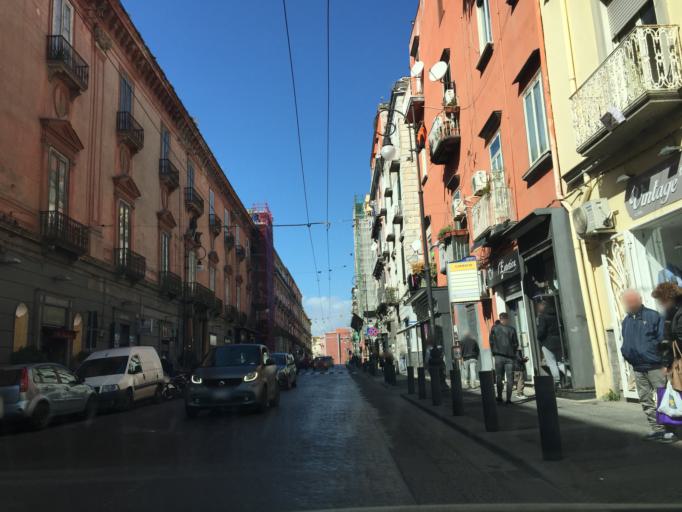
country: IT
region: Campania
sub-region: Provincia di Napoli
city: Portici
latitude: 40.8147
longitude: 14.3358
